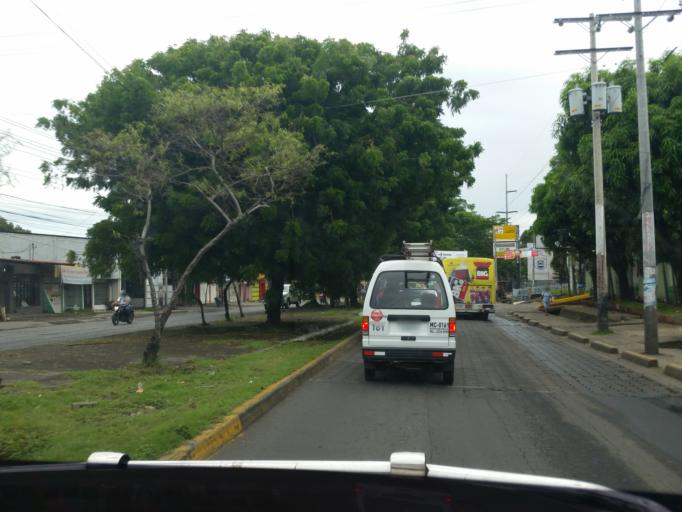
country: NI
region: Managua
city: Managua
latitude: 12.1170
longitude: -86.2508
